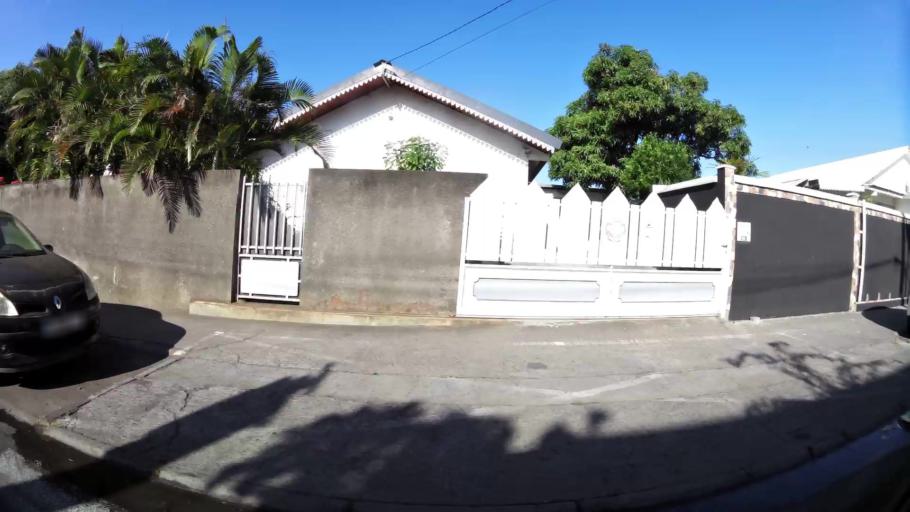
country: RE
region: Reunion
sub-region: Reunion
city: Saint-Louis
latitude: -21.2896
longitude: 55.4105
